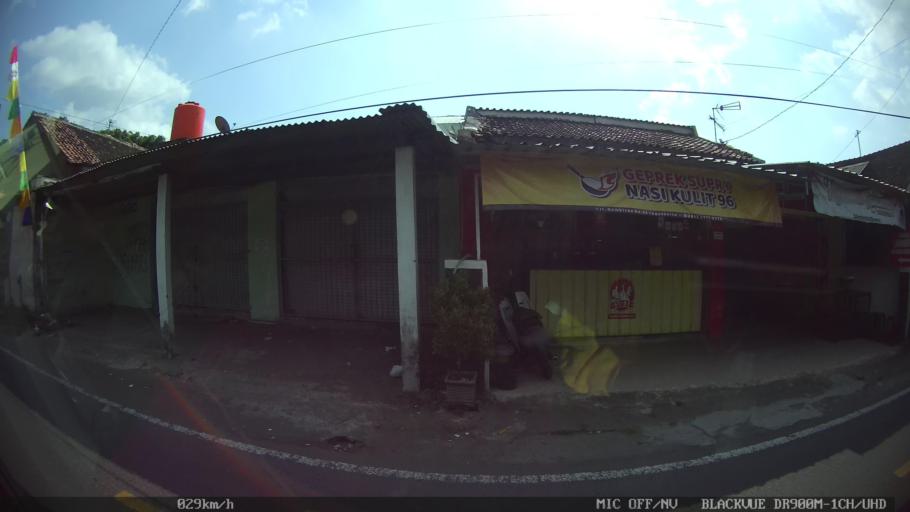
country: ID
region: Daerah Istimewa Yogyakarta
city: Yogyakarta
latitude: -7.8229
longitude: 110.3903
